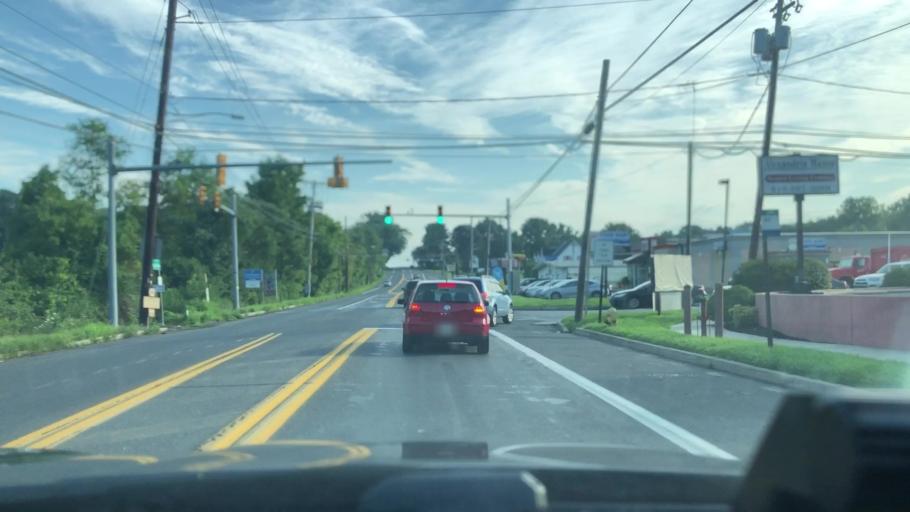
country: US
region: Pennsylvania
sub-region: Northampton County
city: Middletown
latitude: 40.6685
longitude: -75.3485
